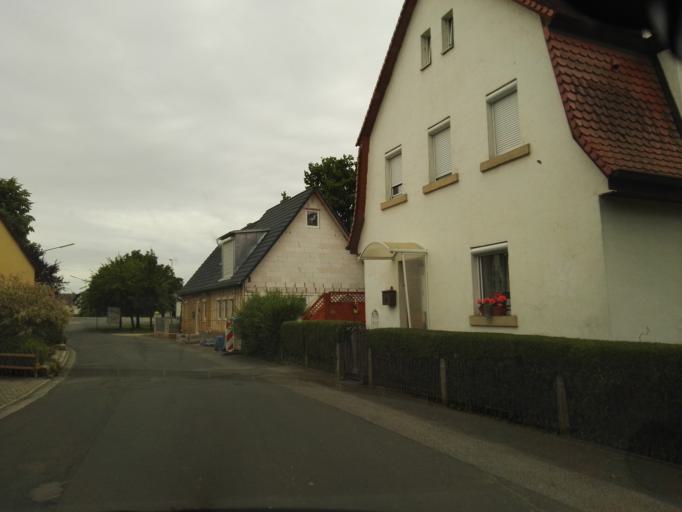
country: DE
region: Bavaria
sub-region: Upper Franconia
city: Redwitz an der Rodach
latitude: 50.1737
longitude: 11.1997
